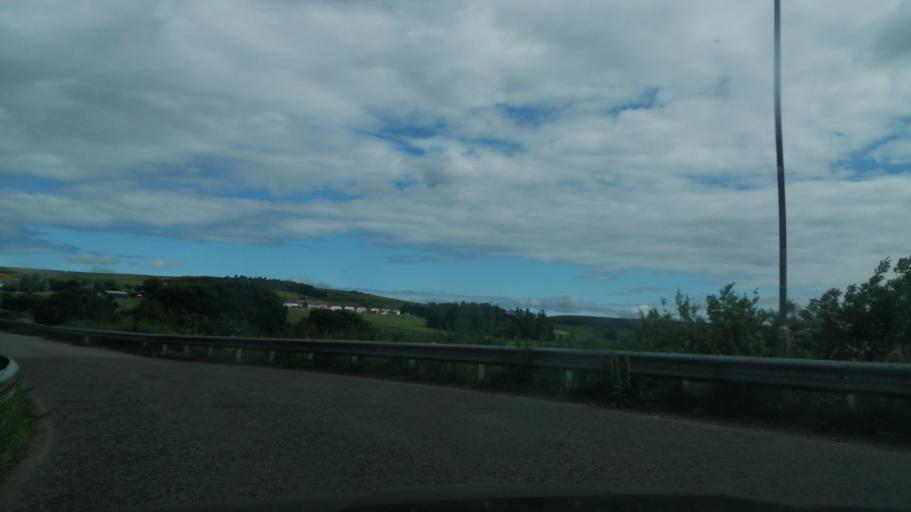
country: GB
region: Scotland
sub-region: Moray
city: Keith
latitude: 57.5524
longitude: -2.9462
